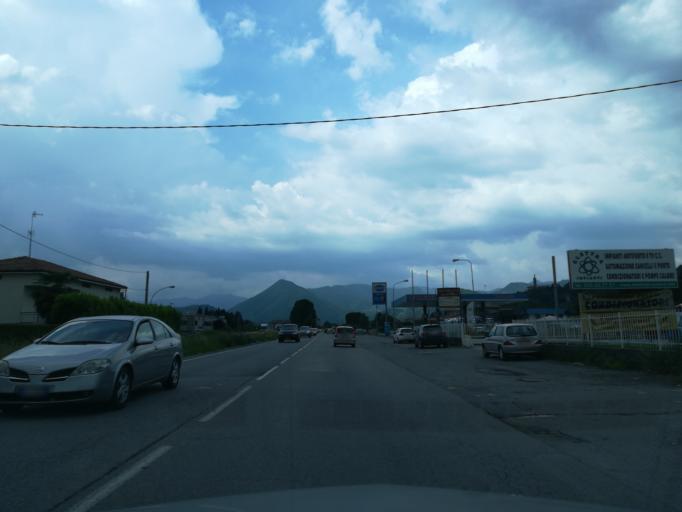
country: IT
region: Lombardy
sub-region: Provincia di Bergamo
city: Scano al Brembo
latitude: 45.7222
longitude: 9.6099
